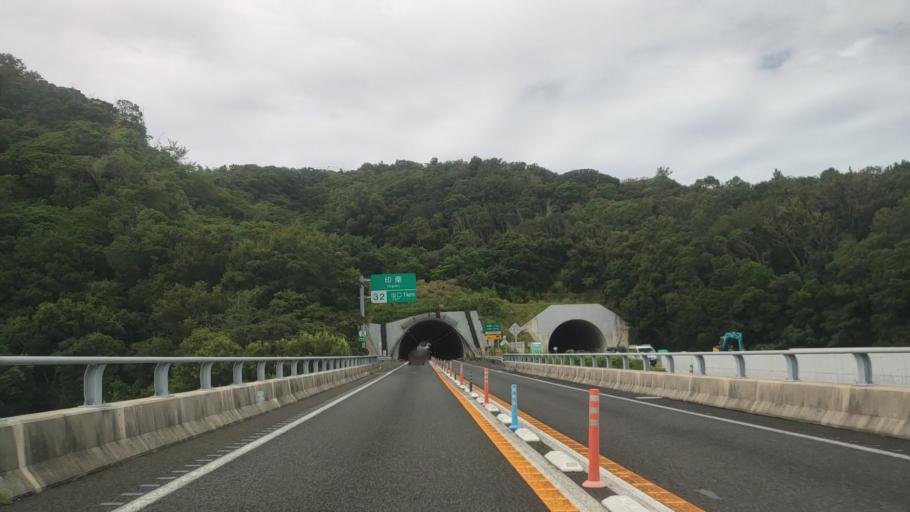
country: JP
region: Wakayama
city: Gobo
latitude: 33.8170
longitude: 135.2276
